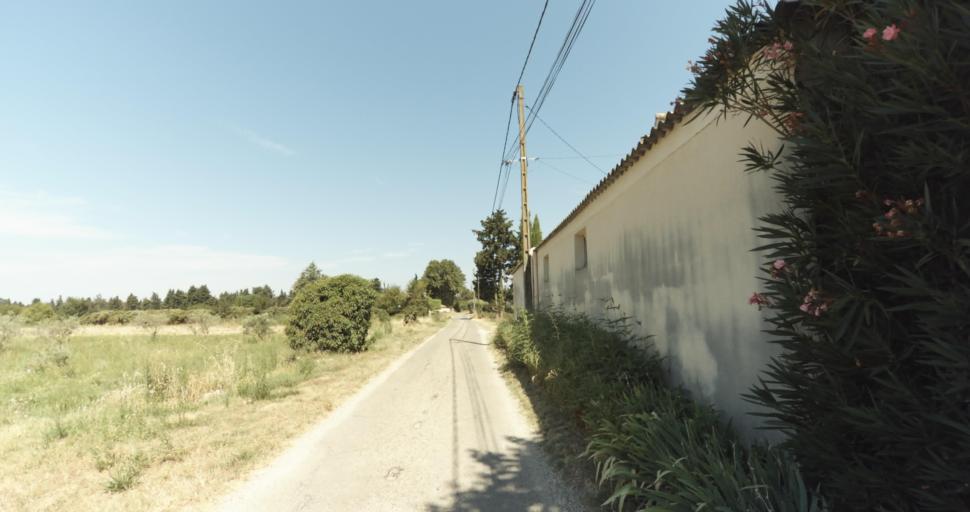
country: FR
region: Provence-Alpes-Cote d'Azur
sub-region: Departement du Vaucluse
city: Monteux
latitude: 44.0140
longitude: 5.0178
